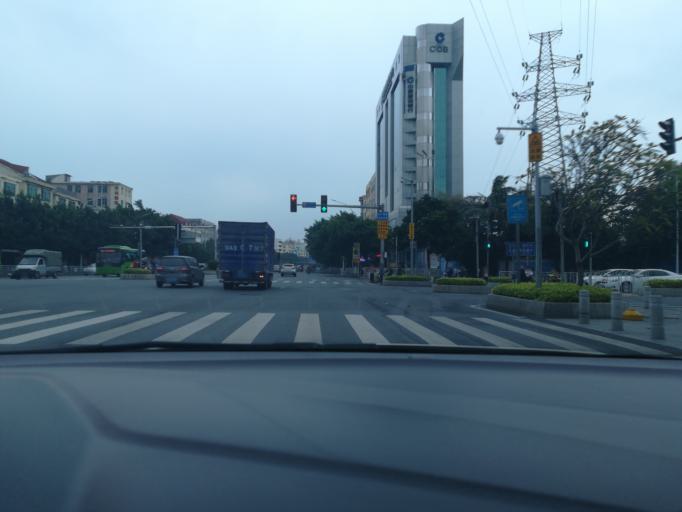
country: CN
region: Guangdong
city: Nansha
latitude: 22.8031
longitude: 113.5409
